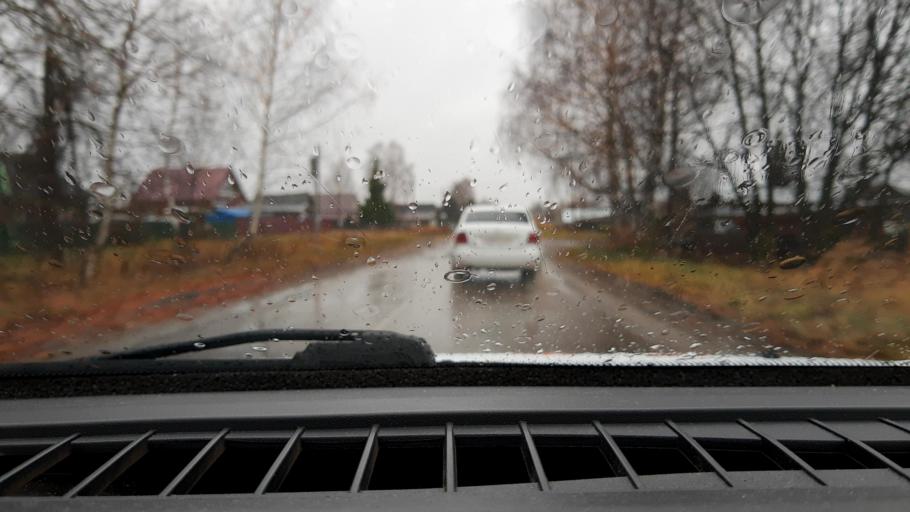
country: RU
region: Nizjnij Novgorod
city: Linda
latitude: 56.6849
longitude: 44.2019
